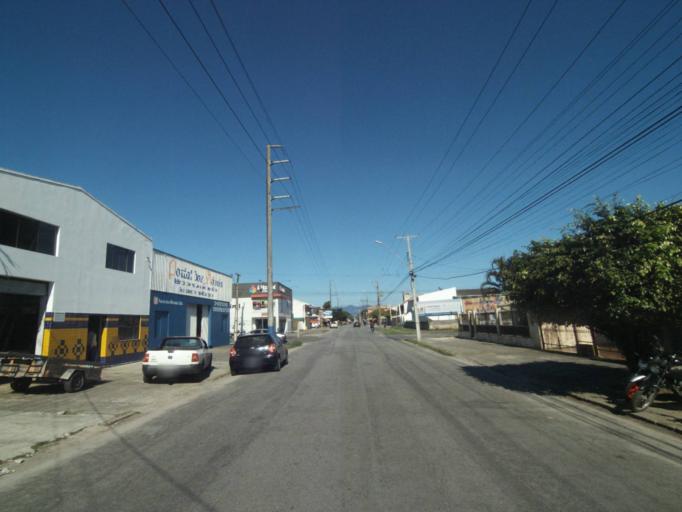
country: BR
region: Parana
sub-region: Paranagua
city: Paranagua
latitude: -25.5241
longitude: -48.5220
